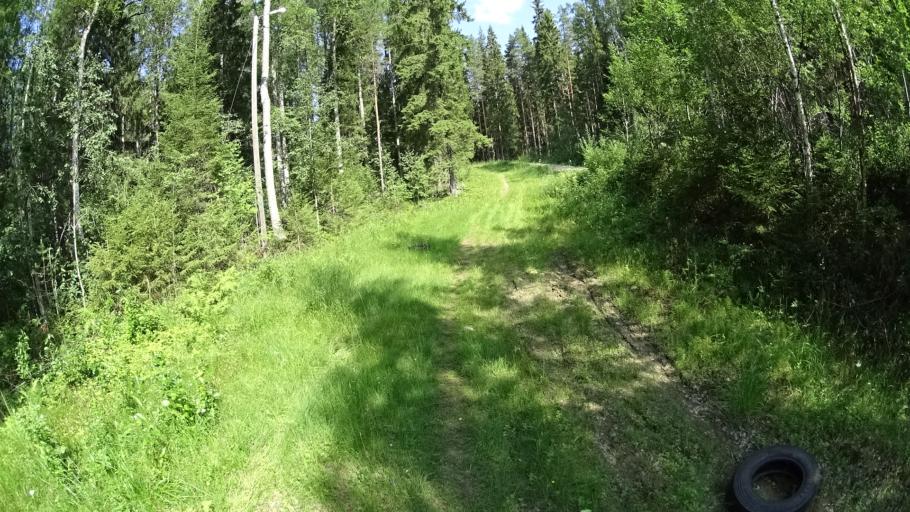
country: FI
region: North Karelia
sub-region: Pielisen Karjala
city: Lieksa
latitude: 63.1227
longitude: 29.8055
